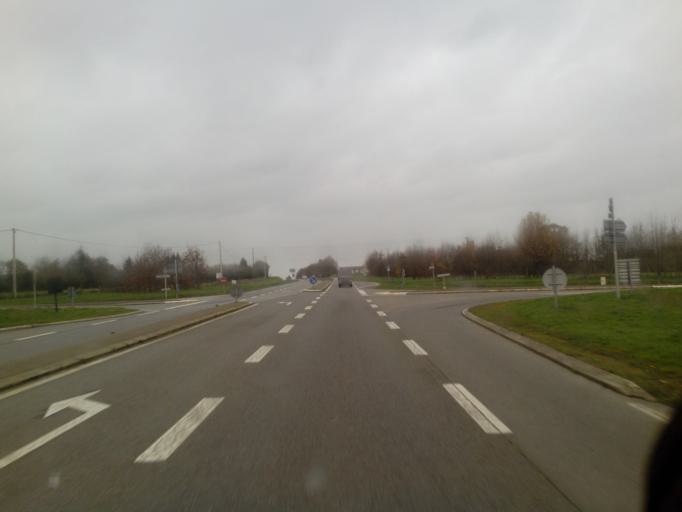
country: FR
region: Brittany
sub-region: Departement d'Ille-et-Vilaine
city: Chevaigne
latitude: 48.2339
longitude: -1.6219
